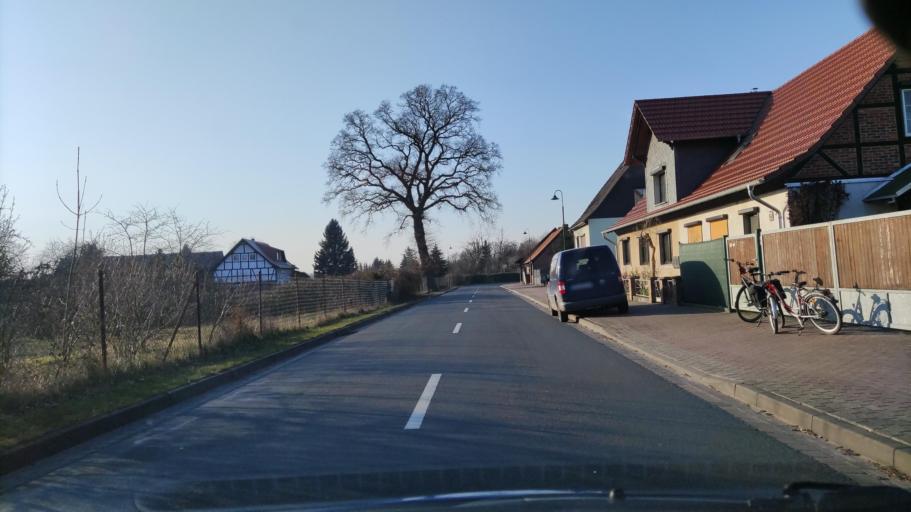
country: DE
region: Brandenburg
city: Cumlosen
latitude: 52.9693
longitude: 11.6255
